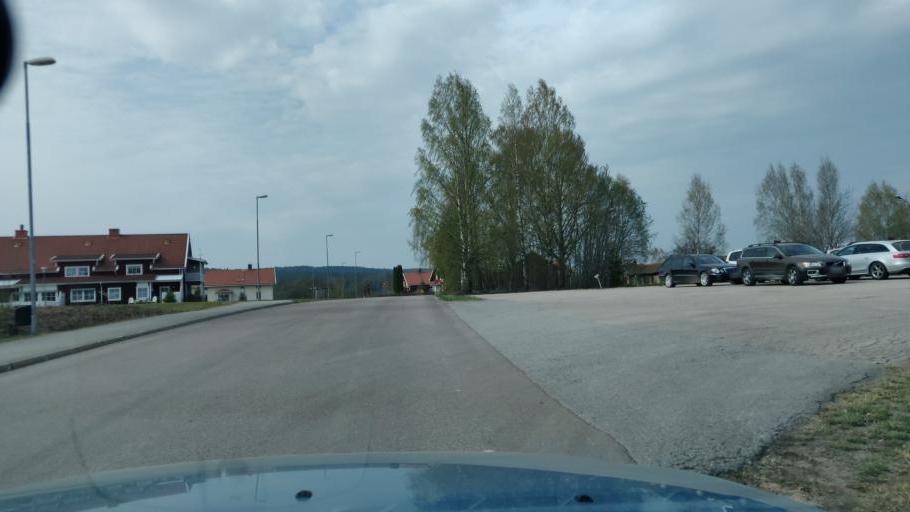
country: SE
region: Vaermland
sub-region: Munkfors Kommun
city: Munkfors
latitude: 59.8397
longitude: 13.5443
